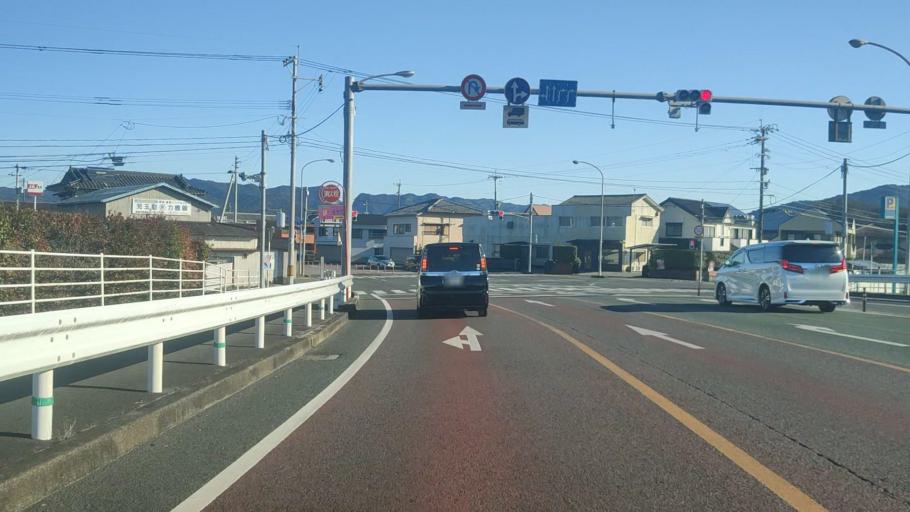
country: JP
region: Miyazaki
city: Nobeoka
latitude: 32.5988
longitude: 131.6812
